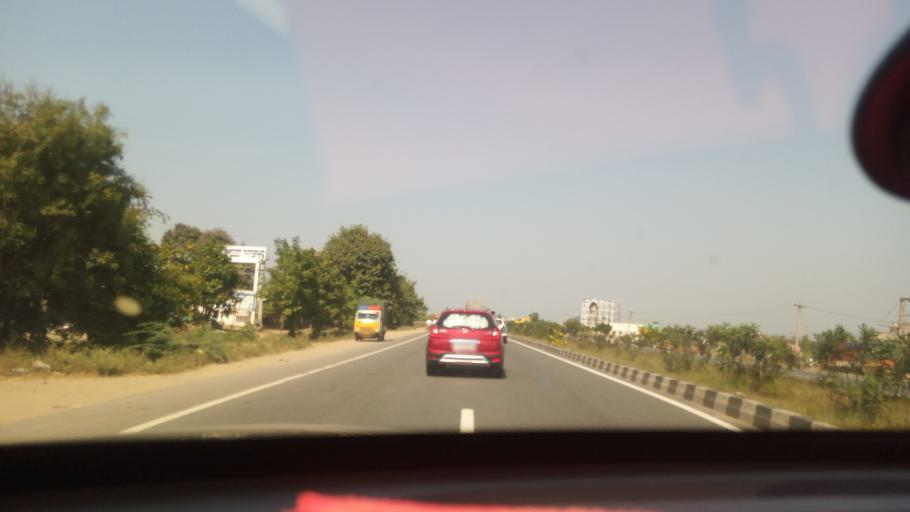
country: IN
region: Tamil Nadu
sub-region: Dharmapuri
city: Dharmapuri
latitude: 12.1820
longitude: 78.1744
